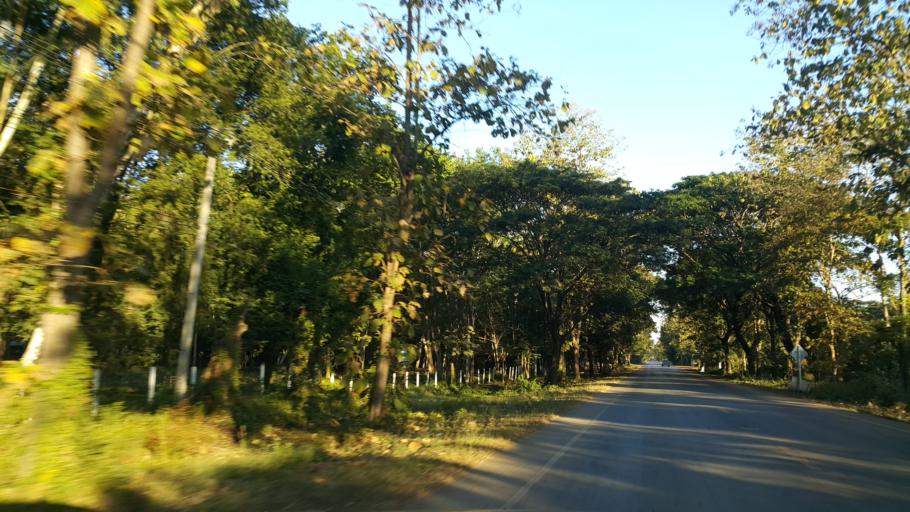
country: TH
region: Sukhothai
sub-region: Amphoe Si Satchanalai
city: Si Satchanalai
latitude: 17.5515
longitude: 99.8824
